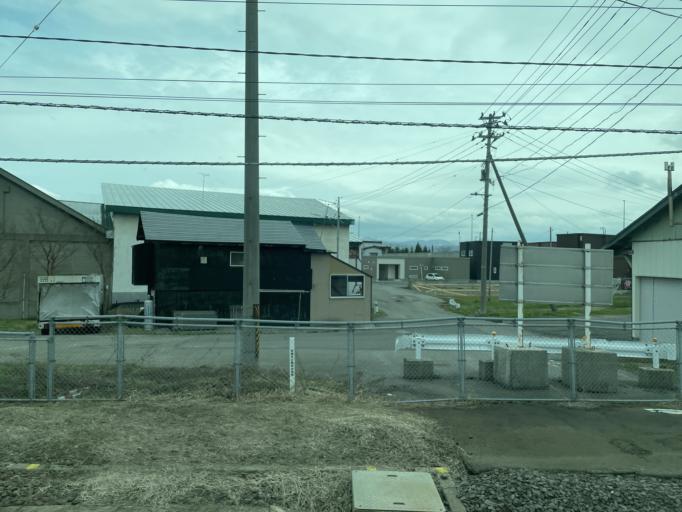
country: JP
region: Aomori
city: Namioka
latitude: 40.7088
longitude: 140.5795
